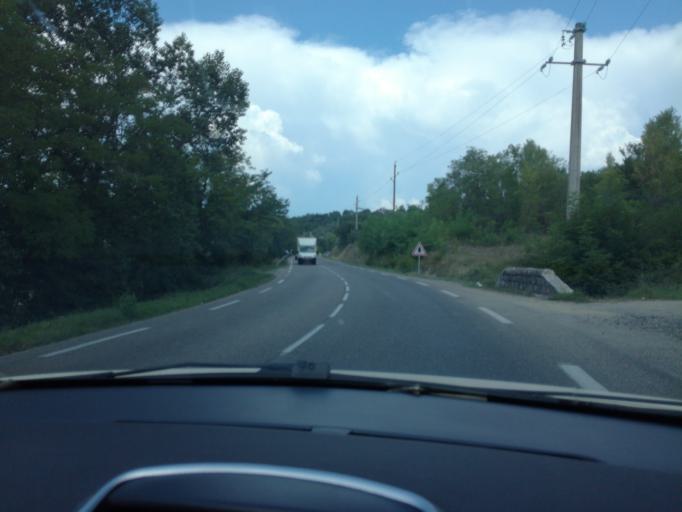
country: FR
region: Rhone-Alpes
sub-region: Departement de l'Ardeche
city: Ruoms
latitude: 44.4899
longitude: 4.3813
